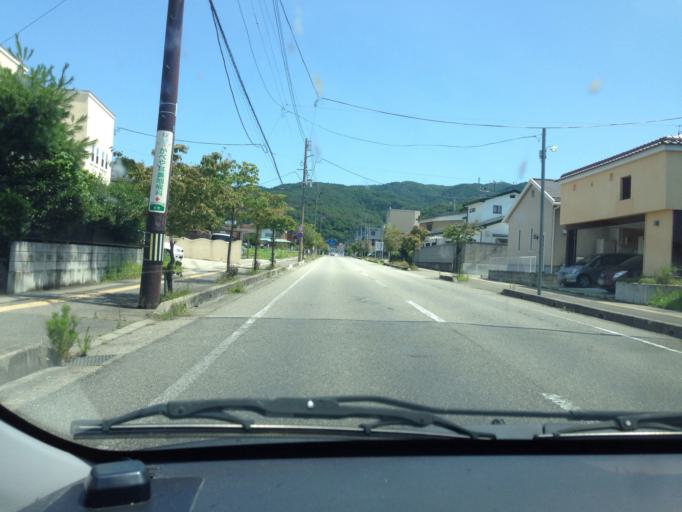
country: JP
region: Fukushima
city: Kitakata
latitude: 37.4989
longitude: 139.9387
